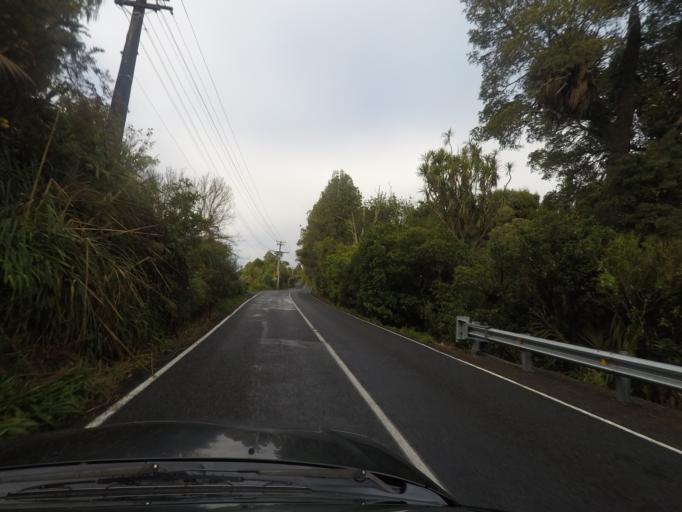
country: NZ
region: Auckland
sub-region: Auckland
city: Titirangi
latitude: -36.9213
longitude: 174.5843
